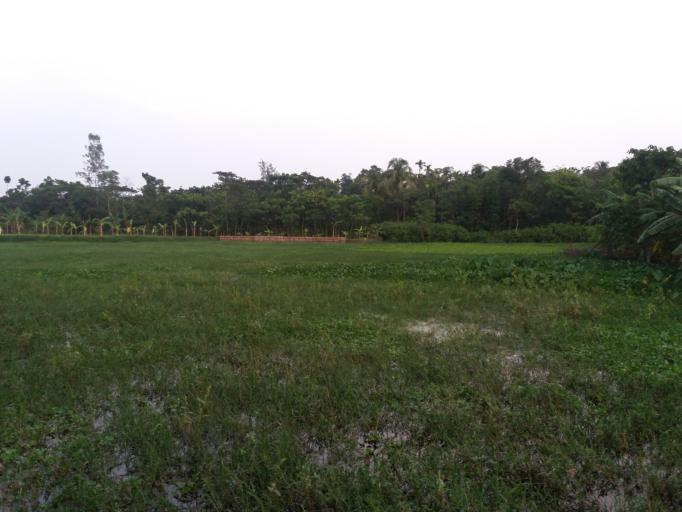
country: BD
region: Chittagong
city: Feni
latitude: 22.9348
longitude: 91.3464
